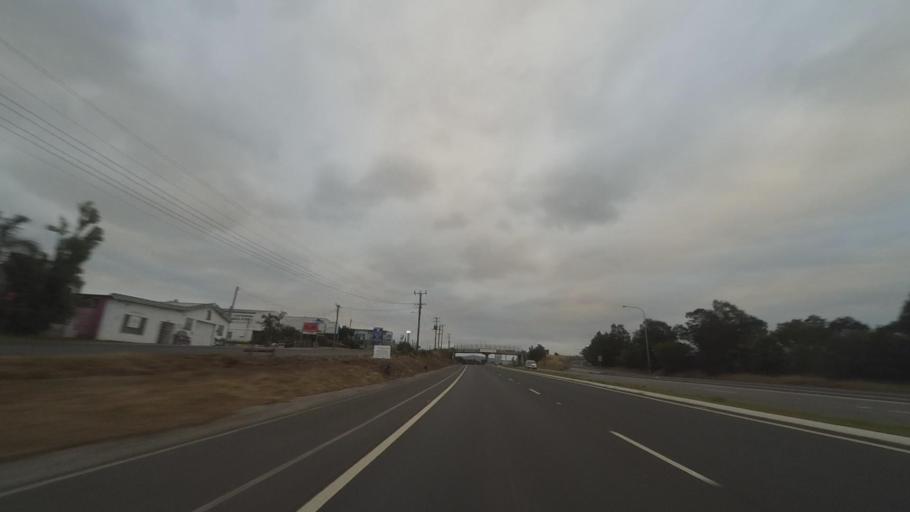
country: AU
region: New South Wales
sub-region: Shellharbour
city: Albion Park Rail
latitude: -34.5437
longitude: 150.7850
